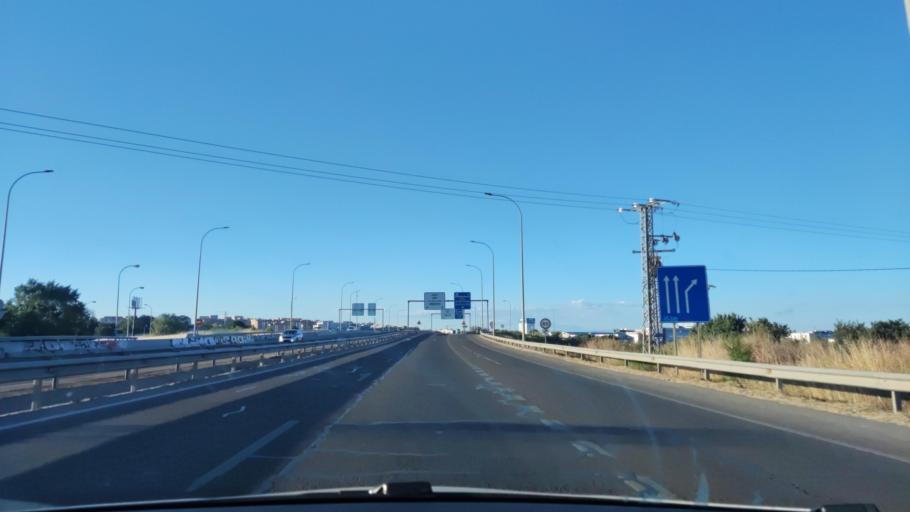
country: ES
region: Madrid
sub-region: Provincia de Madrid
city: Leganes
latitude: 40.3499
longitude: -3.7533
